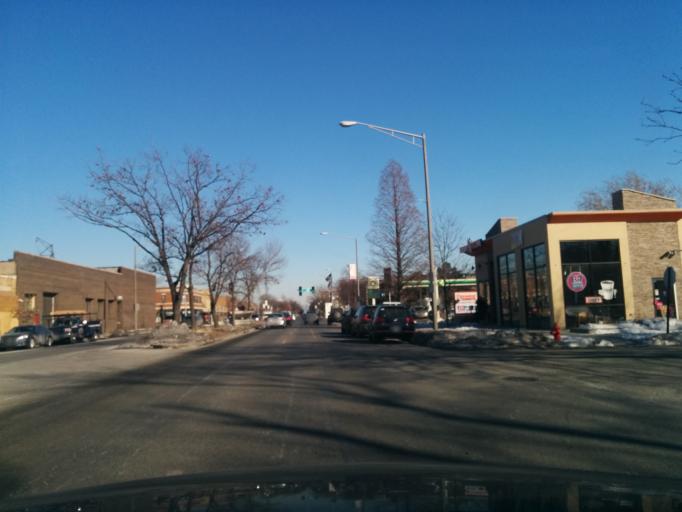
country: US
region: Illinois
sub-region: Cook County
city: Oak Park
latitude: 41.8800
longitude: -87.7811
